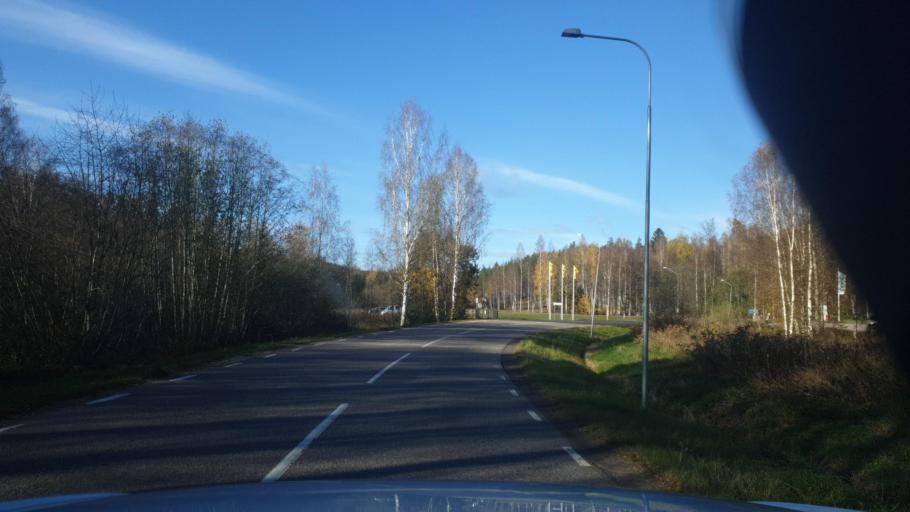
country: SE
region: Vaermland
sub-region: Arvika Kommun
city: Arvika
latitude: 59.6626
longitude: 12.8831
